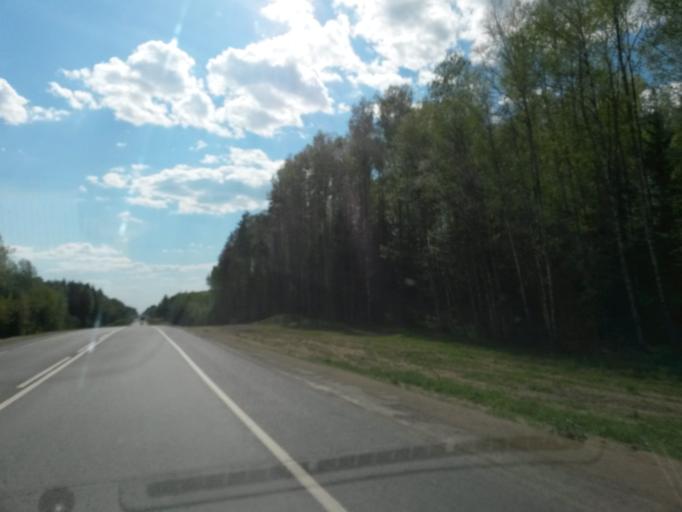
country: RU
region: Jaroslavl
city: Petrovsk
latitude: 56.9185
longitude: 39.1353
